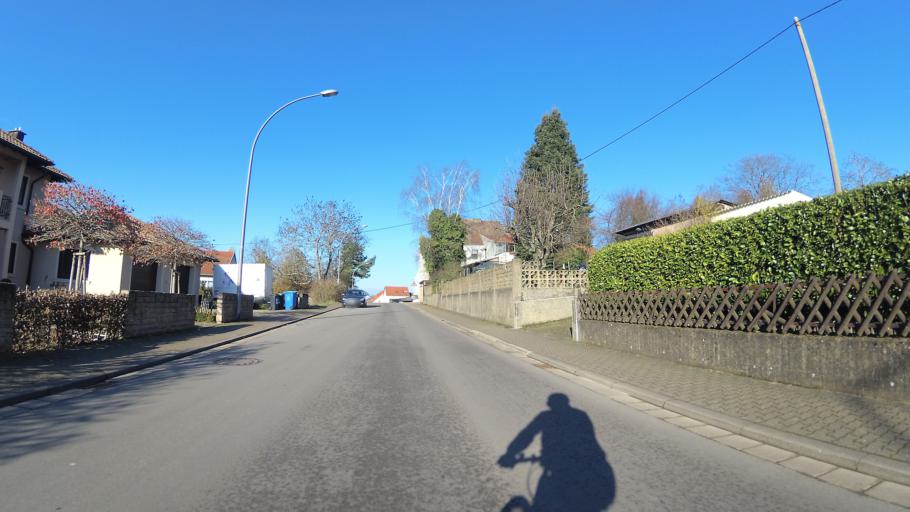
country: DE
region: Saarland
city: Saarlouis
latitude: 49.2991
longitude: 6.7427
